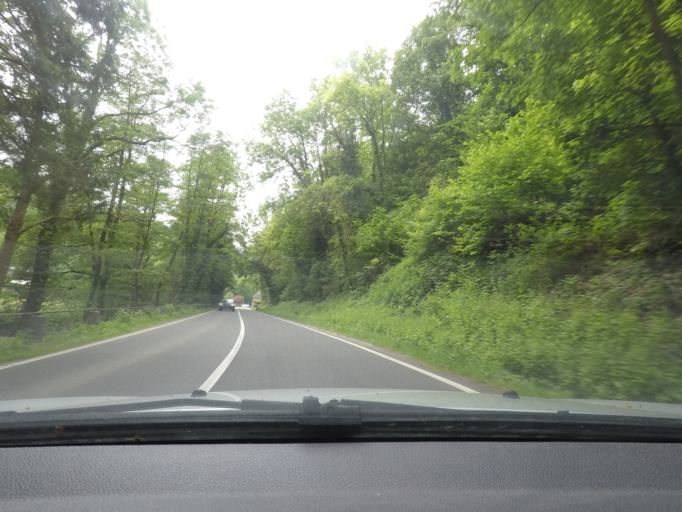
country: BE
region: Wallonia
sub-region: Province de Namur
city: Assesse
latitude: 50.4441
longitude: 5.0120
